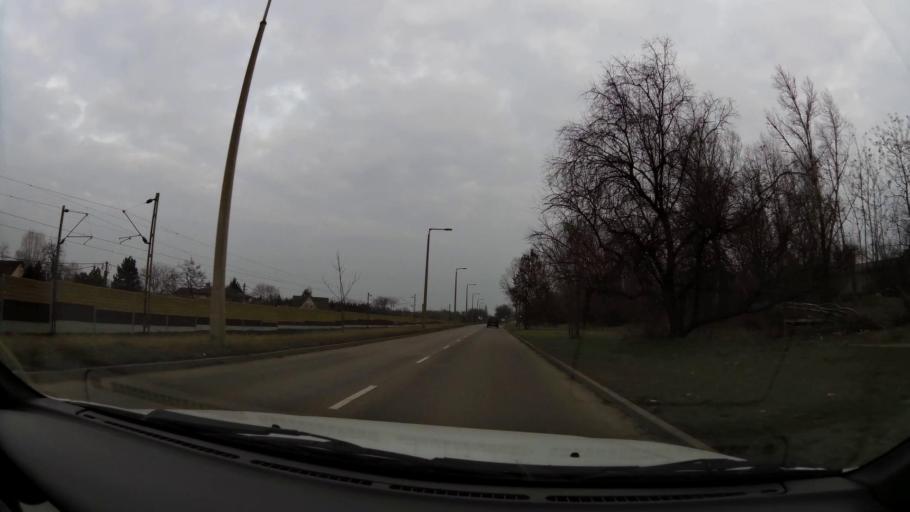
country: HU
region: Budapest
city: Budapest X. keruelet
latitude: 47.4841
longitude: 19.1986
